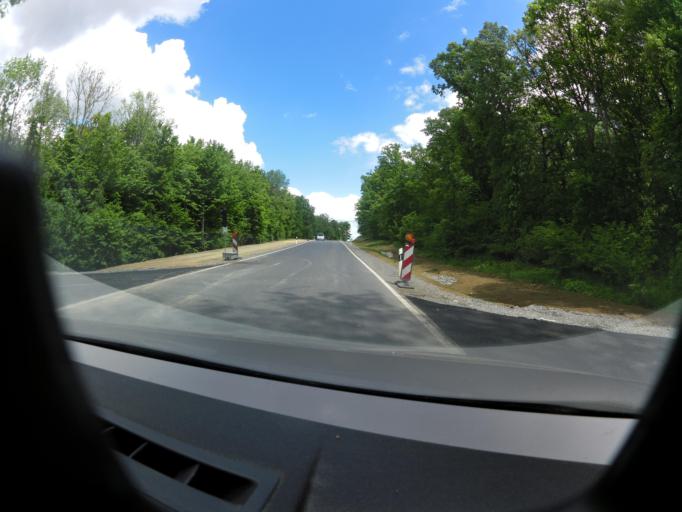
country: DE
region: Bavaria
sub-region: Regierungsbezirk Unterfranken
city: Schwanfeld
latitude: 49.9355
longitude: 10.1371
